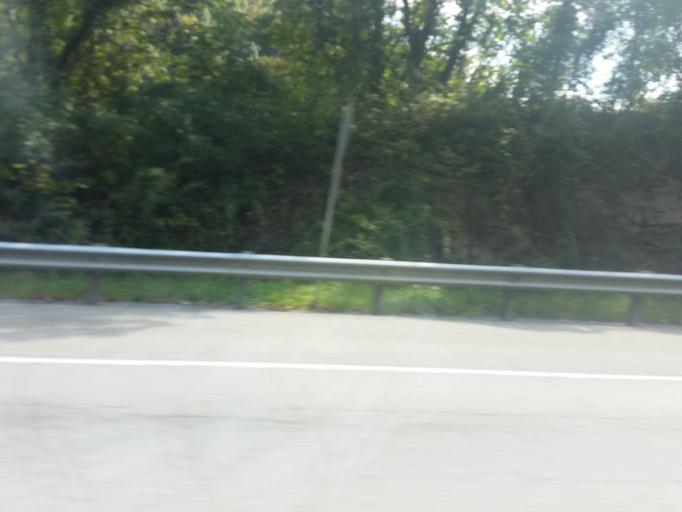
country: US
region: Kentucky
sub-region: Bell County
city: Pineville
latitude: 36.7475
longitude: -83.6902
